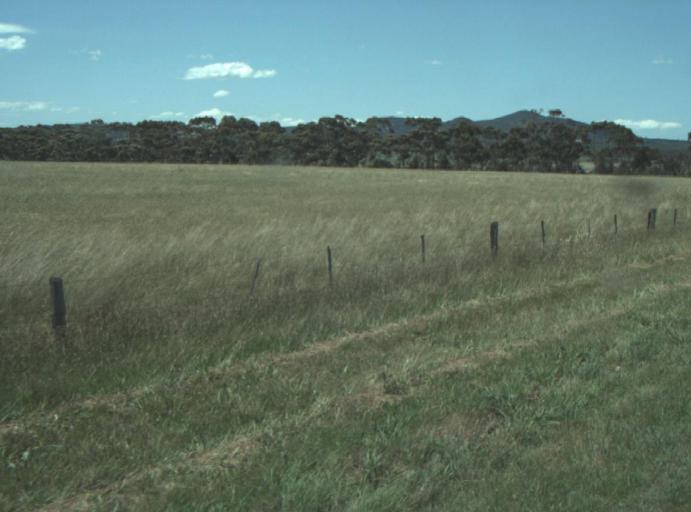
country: AU
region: Victoria
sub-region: Greater Geelong
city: Lara
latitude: -37.9585
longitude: 144.3486
